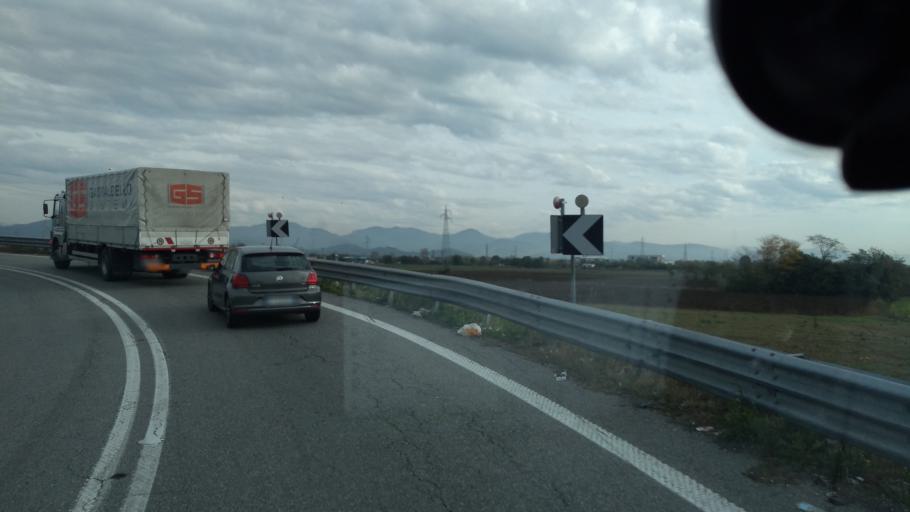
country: IT
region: Lombardy
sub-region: Provincia di Bergamo
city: Grassobbio
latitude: 45.6360
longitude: 9.7131
